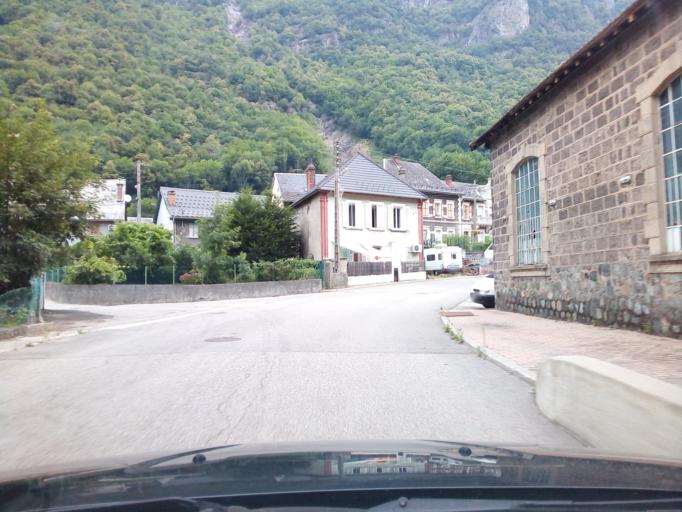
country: FR
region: Rhone-Alpes
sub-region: Departement de l'Isere
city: Livet-et-Gavet
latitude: 45.1075
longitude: 5.9332
